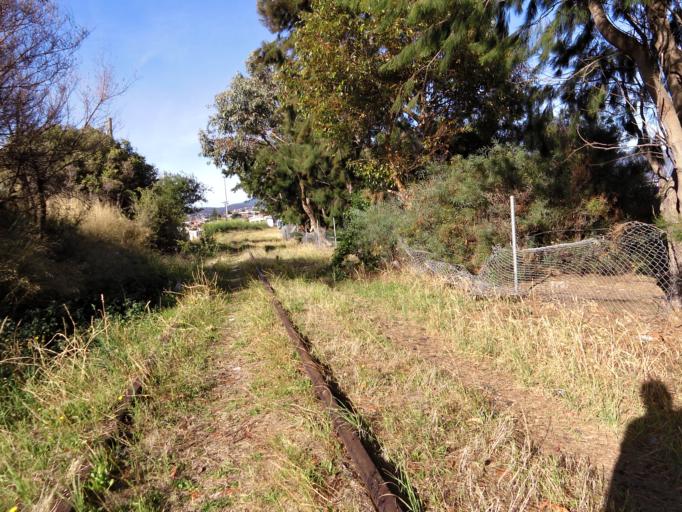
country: AU
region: Tasmania
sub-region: Glenorchy
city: Lutana
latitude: -42.8357
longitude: 147.3041
